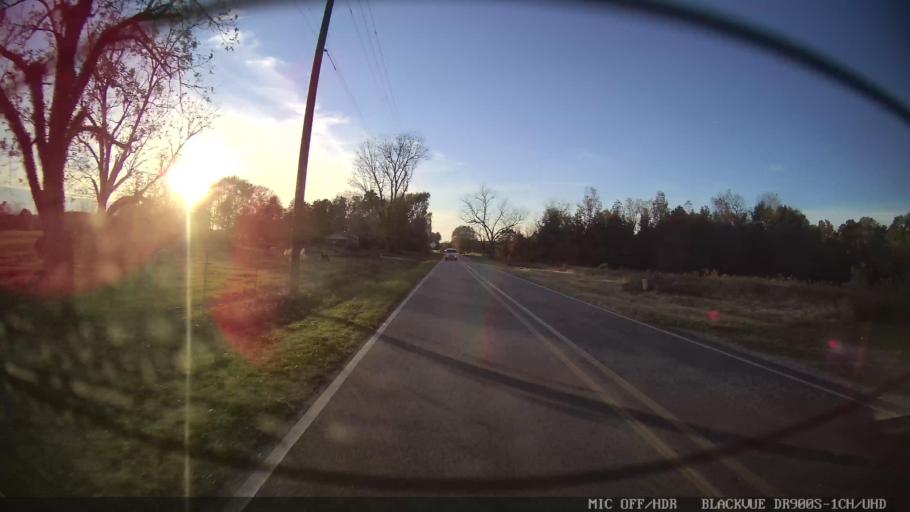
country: US
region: Mississippi
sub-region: Lamar County
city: Lumberton
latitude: 30.9973
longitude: -89.3962
